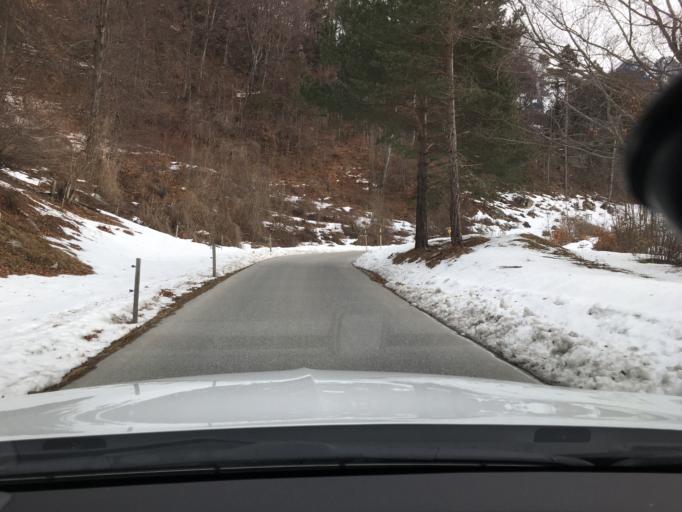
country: CH
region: Grisons
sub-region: Landquart District
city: Maienfeld
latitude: 47.0249
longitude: 9.5261
